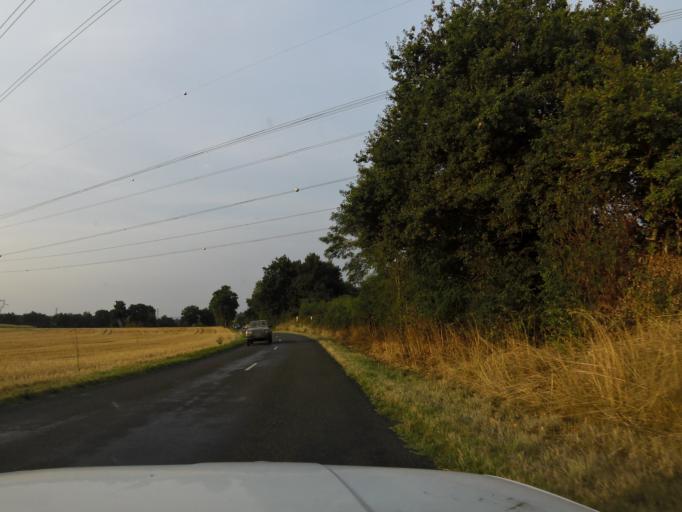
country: FR
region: Rhone-Alpes
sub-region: Departement de l'Ain
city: Saint-Maurice-de-Gourdans
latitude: 45.8427
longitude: 5.1899
